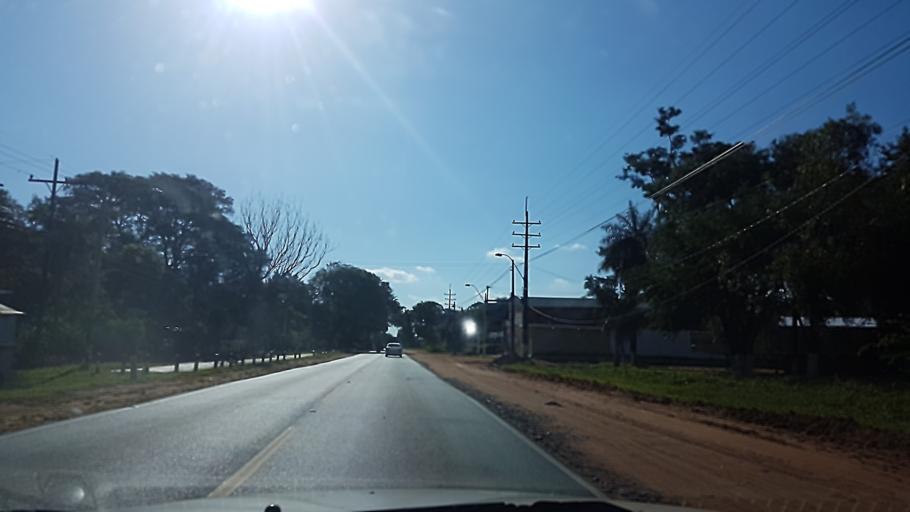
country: PY
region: Central
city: San Antonio
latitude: -25.4483
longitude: -57.5242
